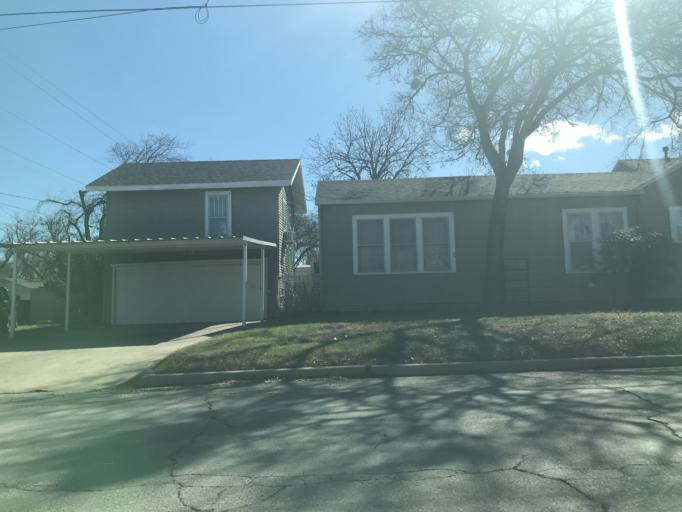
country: US
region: Texas
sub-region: Tom Green County
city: San Angelo
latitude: 31.4475
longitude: -100.4556
